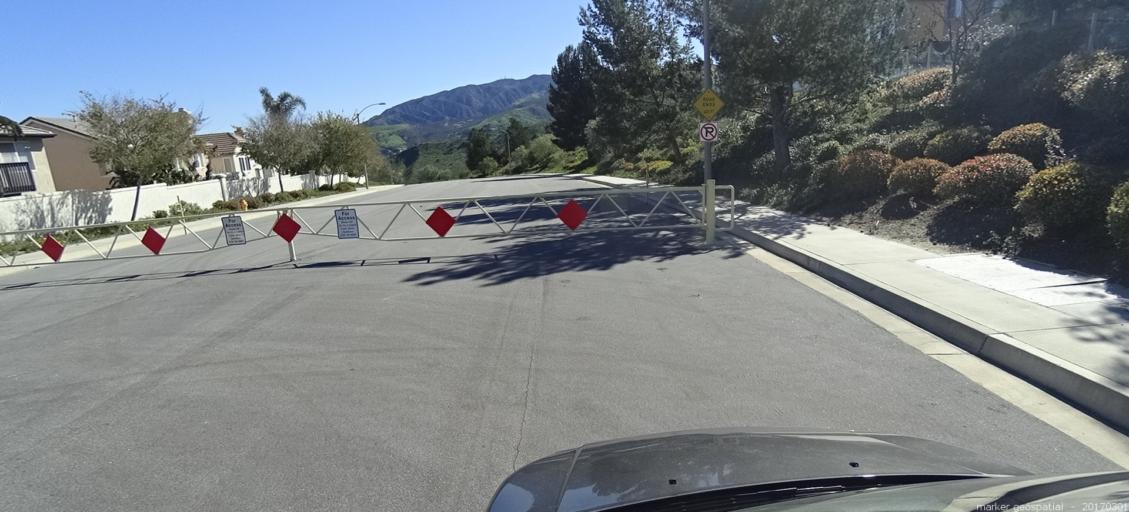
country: US
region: California
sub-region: Orange County
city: Yorba Linda
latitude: 33.8563
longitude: -117.7224
